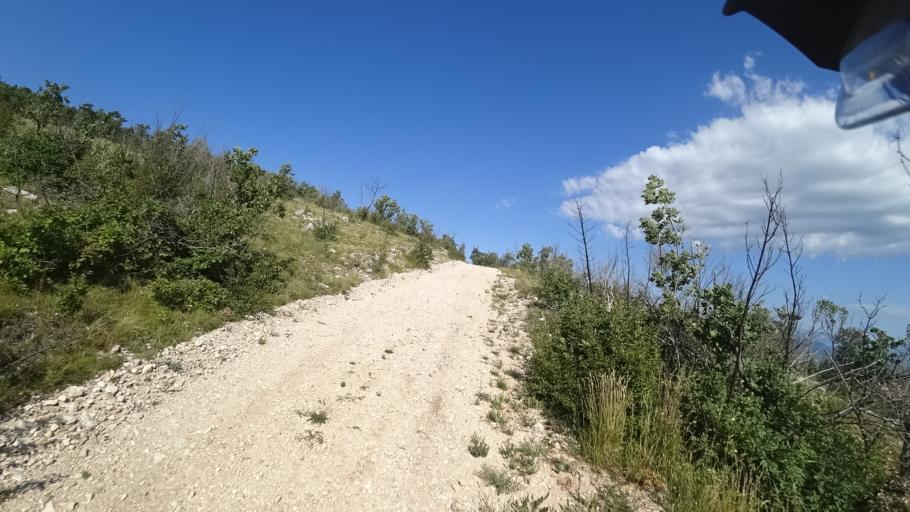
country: HR
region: Sibensko-Kniniska
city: Knin
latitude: 43.9605
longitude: 16.1530
